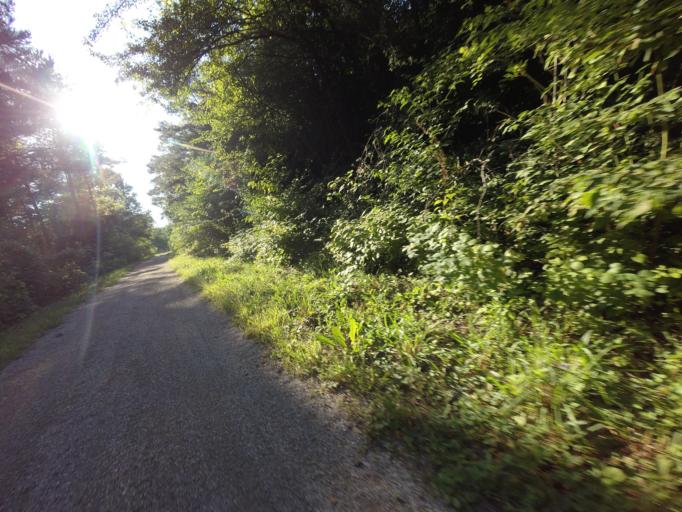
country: CA
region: Ontario
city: Goderich
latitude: 43.7514
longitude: -81.5824
